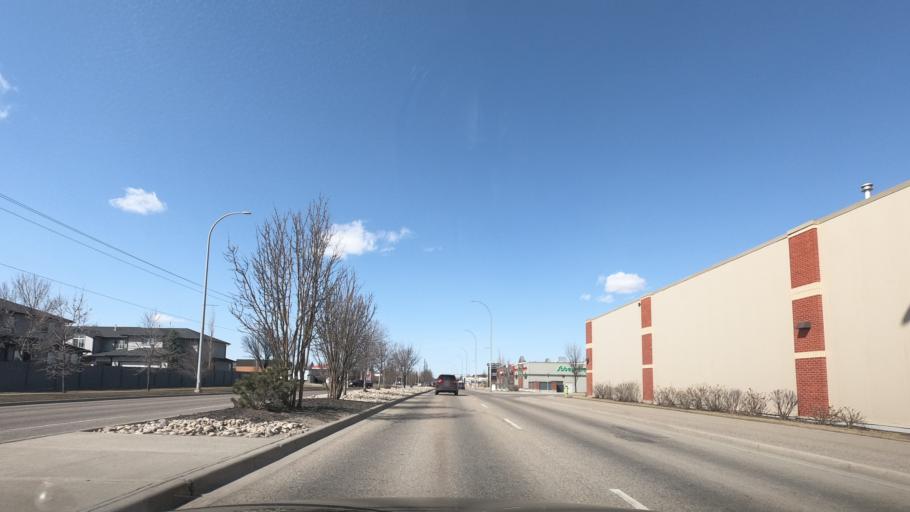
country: CA
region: Alberta
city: Airdrie
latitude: 51.2907
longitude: -114.0251
